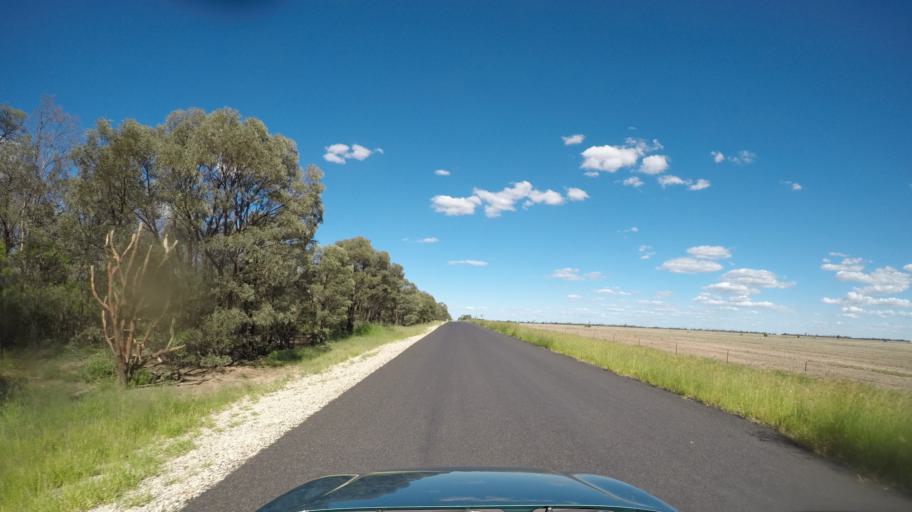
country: AU
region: Queensland
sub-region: Goondiwindi
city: Goondiwindi
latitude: -28.1600
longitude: 150.4021
